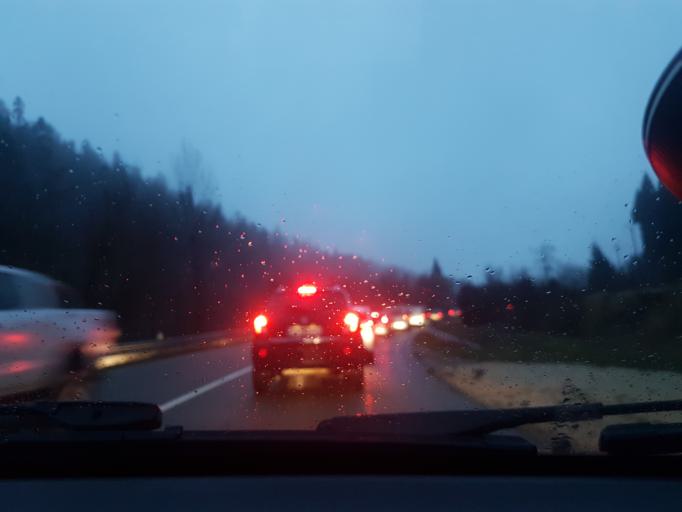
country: FR
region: Franche-Comte
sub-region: Departement du Doubs
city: La Cluse-et-Mijoux
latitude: 46.8819
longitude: 6.3651
